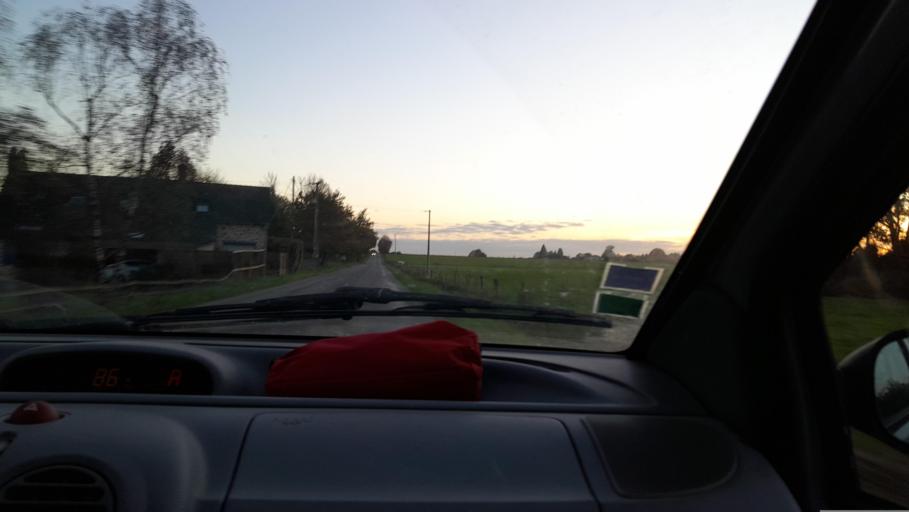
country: FR
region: Pays de la Loire
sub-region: Departement de la Mayenne
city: Ballots
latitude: 47.9296
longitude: -1.0913
